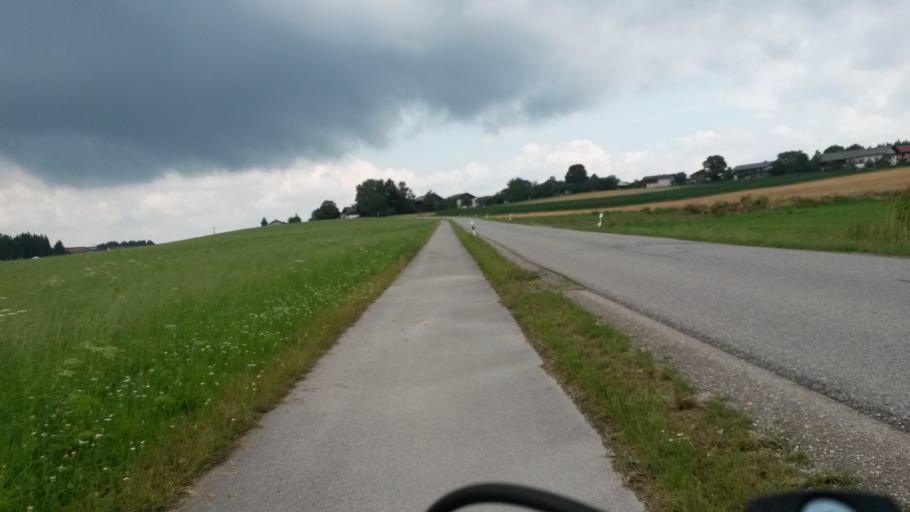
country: DE
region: Bavaria
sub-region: Upper Bavaria
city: Hoslwang
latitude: 47.9618
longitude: 12.3257
